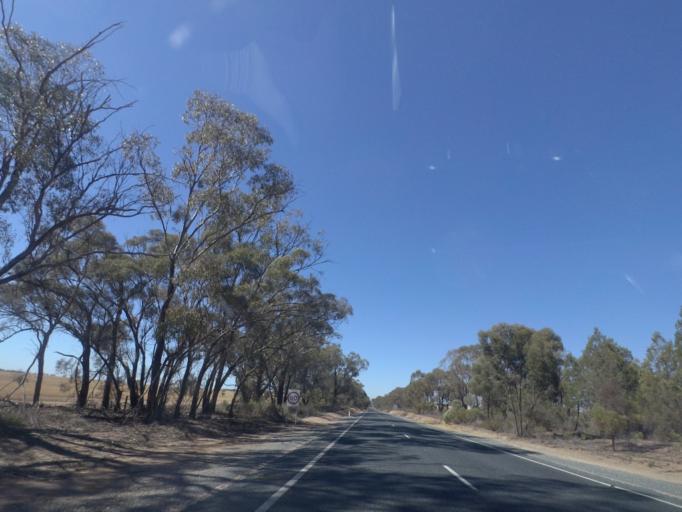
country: AU
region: New South Wales
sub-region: Bland
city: West Wyalong
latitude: -34.1434
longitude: 147.1198
